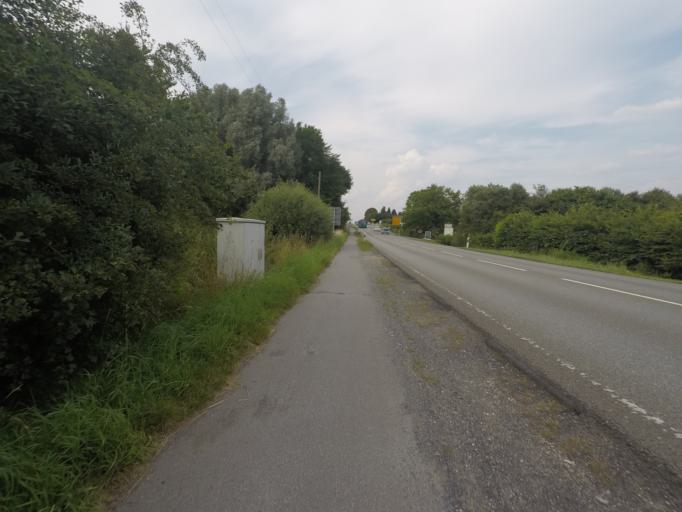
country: DE
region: North Rhine-Westphalia
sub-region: Regierungsbezirk Detmold
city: Herford
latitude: 52.0694
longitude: 8.6133
